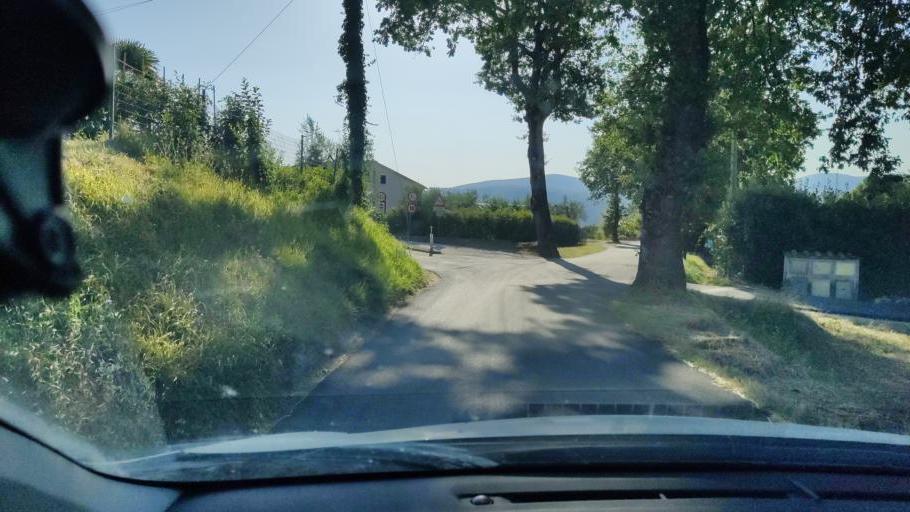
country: IT
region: Umbria
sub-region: Provincia di Terni
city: Amelia
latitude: 42.5400
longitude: 12.4033
